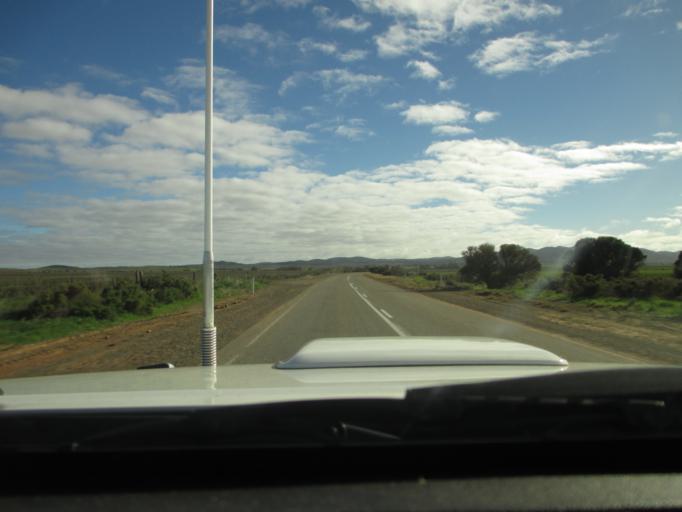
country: AU
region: South Australia
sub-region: Peterborough
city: Peterborough
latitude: -32.6497
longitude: 138.6011
